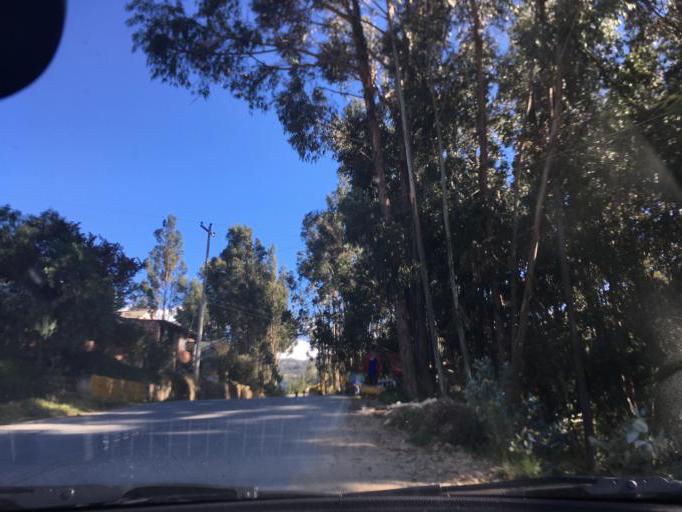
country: CO
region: Boyaca
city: Firavitoba
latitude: 5.5933
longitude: -72.9789
